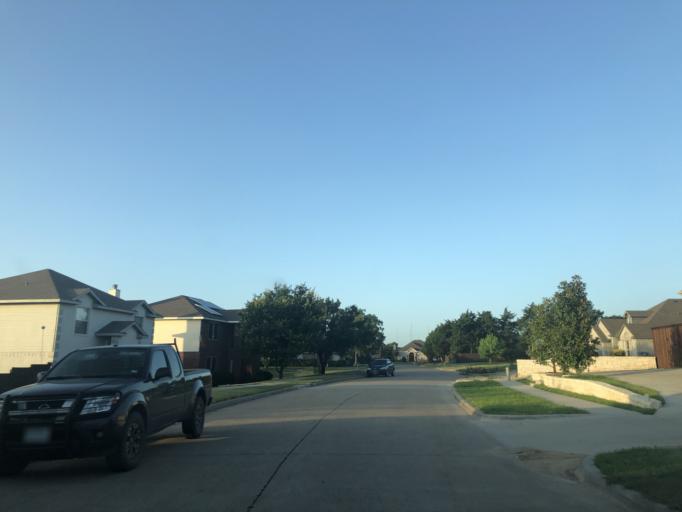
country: US
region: Texas
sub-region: Dallas County
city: Duncanville
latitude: 32.6492
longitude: -96.9552
